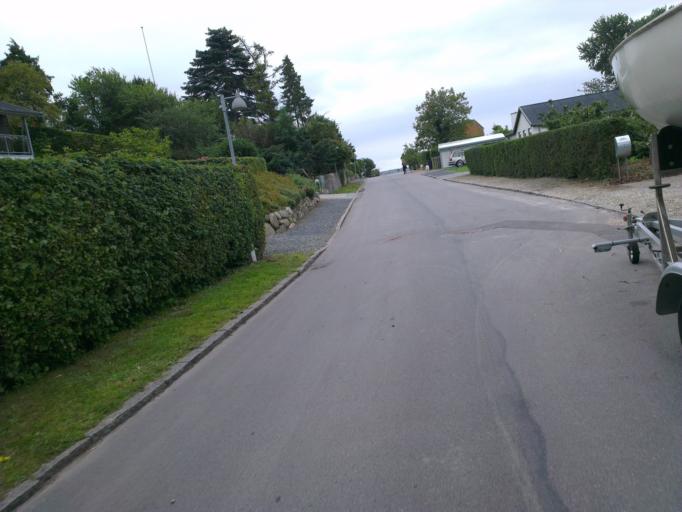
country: DK
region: Capital Region
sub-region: Frederikssund Kommune
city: Frederikssund
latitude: 55.8439
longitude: 12.0465
